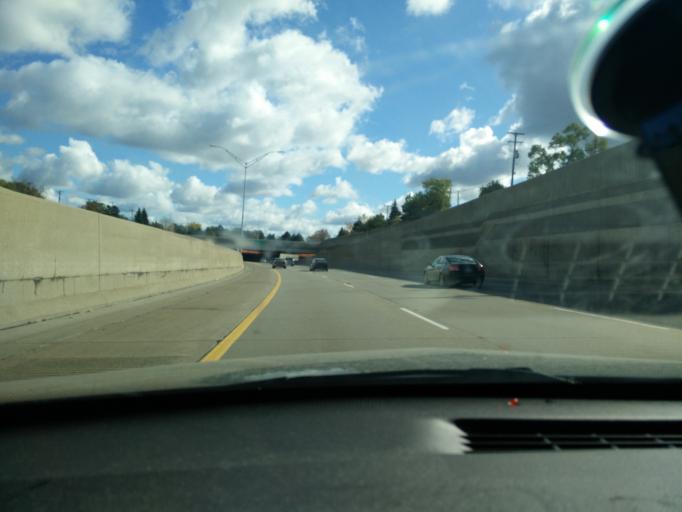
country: US
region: Michigan
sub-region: Oakland County
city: Southfield
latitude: 42.4768
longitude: -83.2000
